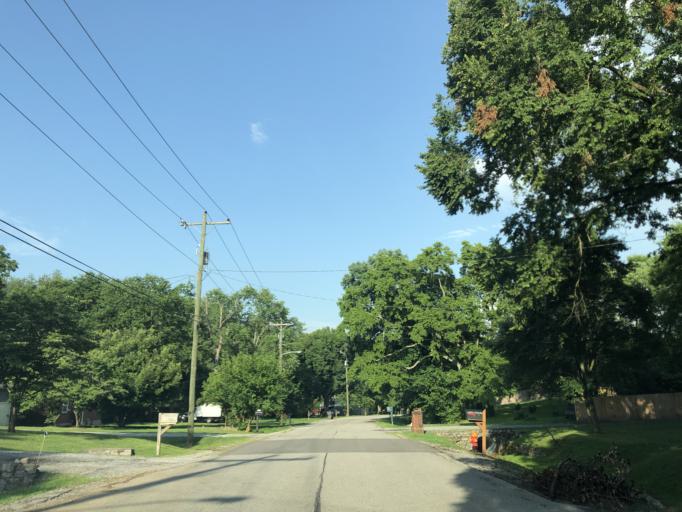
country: US
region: Tennessee
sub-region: Davidson County
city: Lakewood
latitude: 36.1524
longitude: -86.6557
